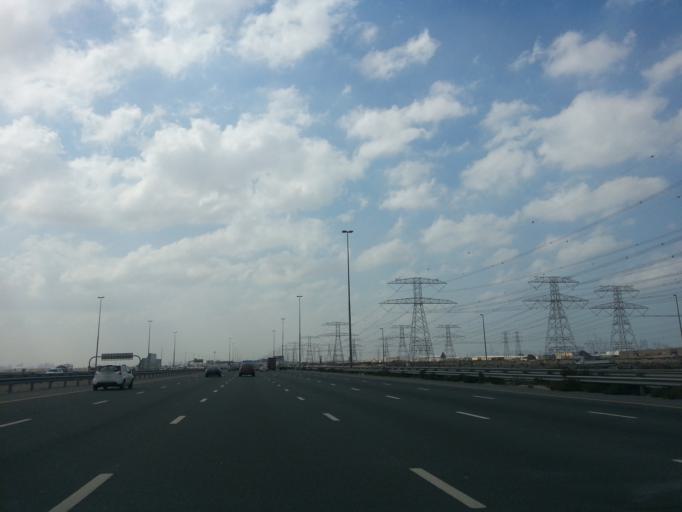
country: AE
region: Dubai
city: Dubai
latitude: 25.1179
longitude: 55.2468
